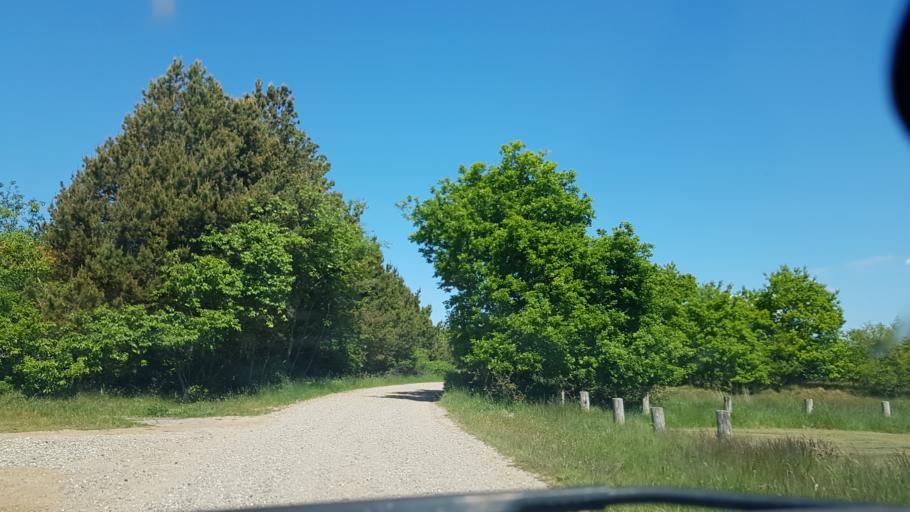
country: DE
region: Schleswig-Holstein
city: List
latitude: 55.1116
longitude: 8.5500
